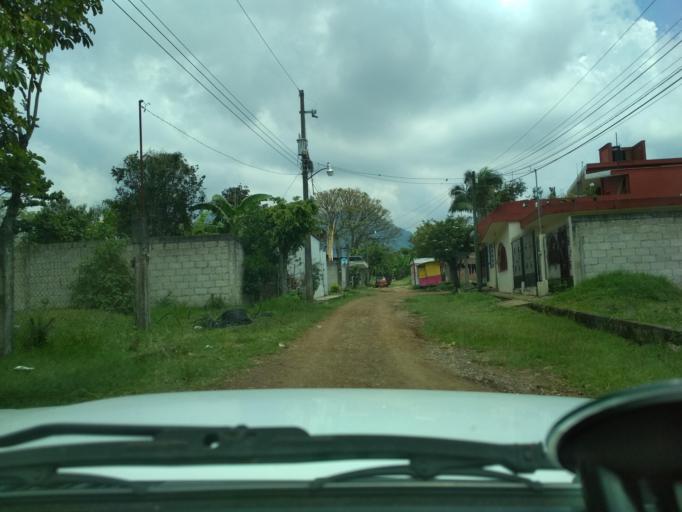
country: MX
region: Veracruz
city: Tocuila
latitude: 18.9530
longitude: -97.0188
